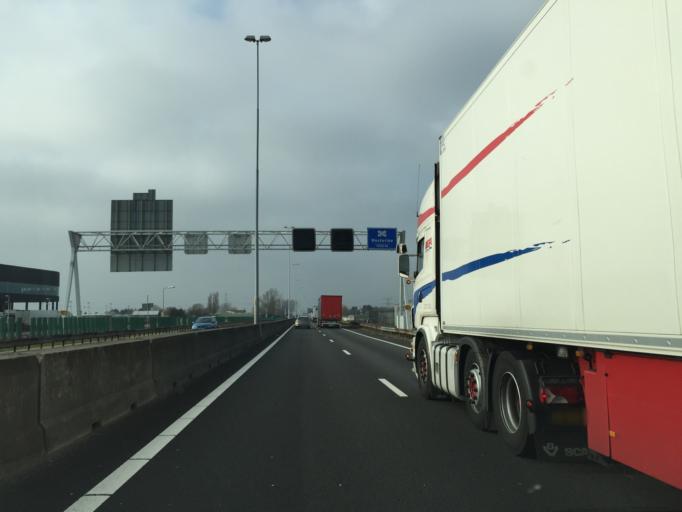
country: NL
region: South Holland
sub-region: Gemeente Westland
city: Maasdijk
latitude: 51.9641
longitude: 4.2241
